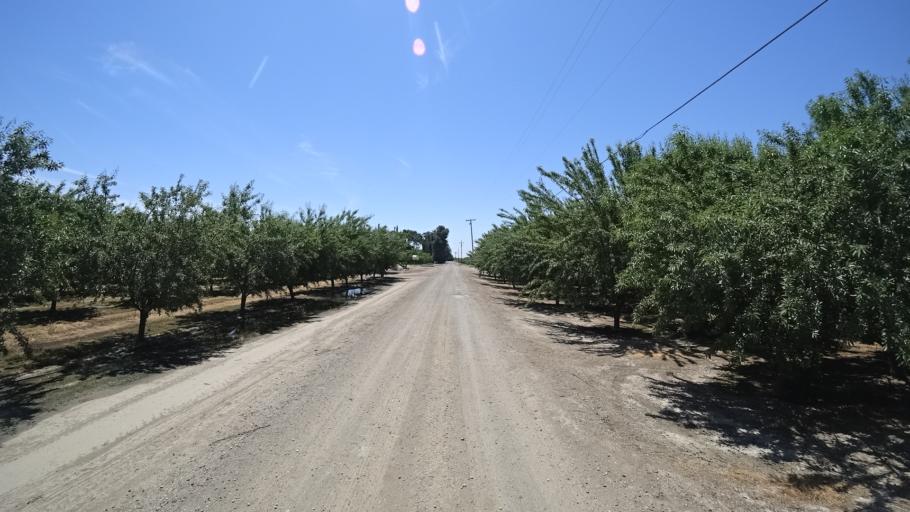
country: US
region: California
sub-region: Kings County
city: Lemoore
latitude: 36.3468
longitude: -119.7673
